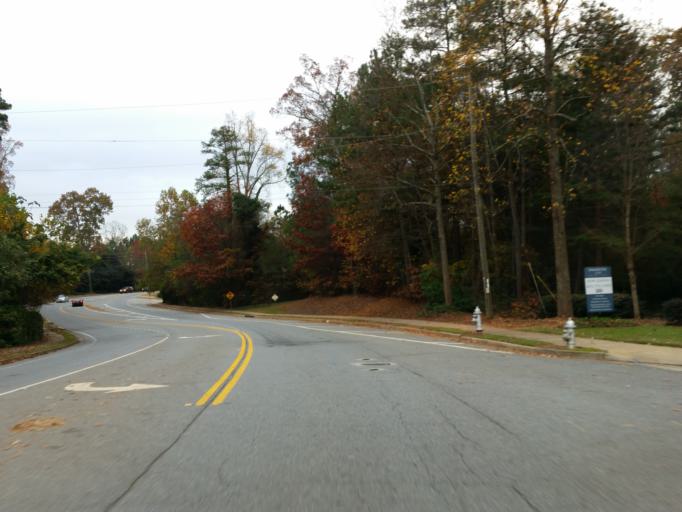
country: US
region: Georgia
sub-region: Fulton County
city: Sandy Springs
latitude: 33.9059
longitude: -84.3686
